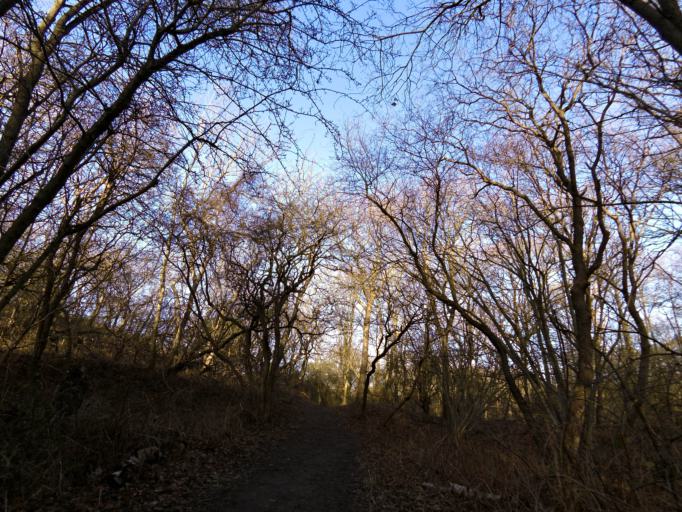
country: NL
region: South Holland
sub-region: Gemeente Hellevoetsluis
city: Nieuw-Helvoet
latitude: 51.8992
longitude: 4.0558
